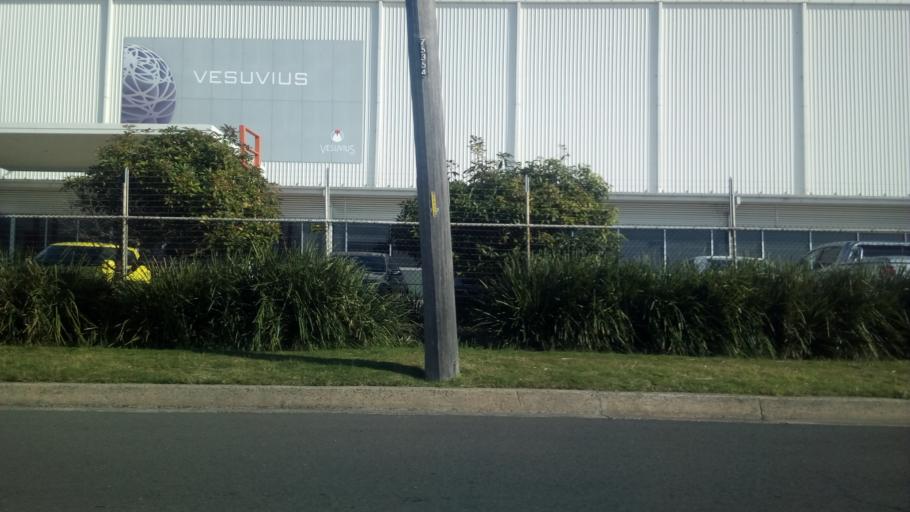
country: AU
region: New South Wales
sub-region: Wollongong
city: Port Kembla
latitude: -34.4794
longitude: 150.9128
